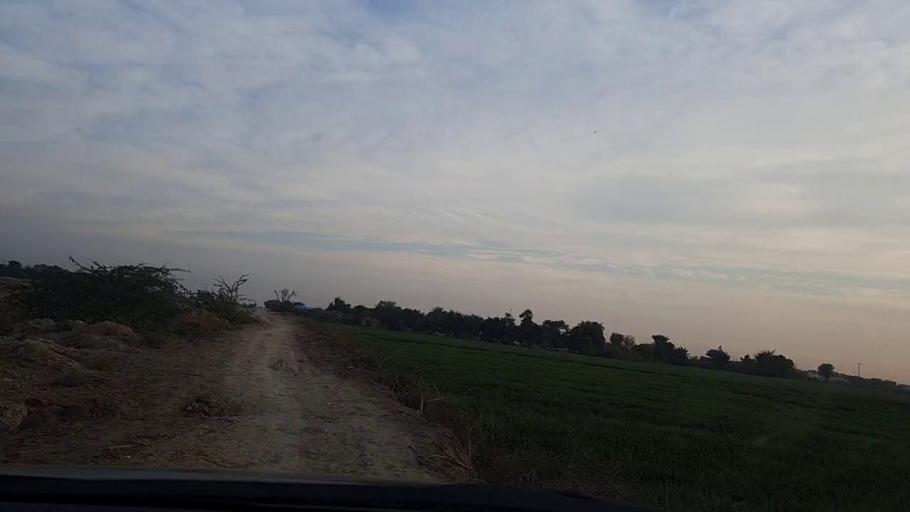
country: PK
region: Sindh
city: Sakrand
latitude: 26.1881
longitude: 68.3371
